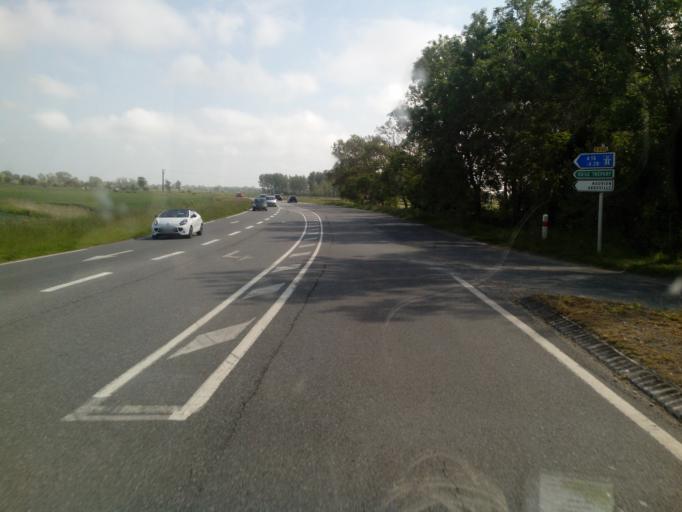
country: FR
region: Picardie
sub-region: Departement de la Somme
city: Rue
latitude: 50.2693
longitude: 1.6548
